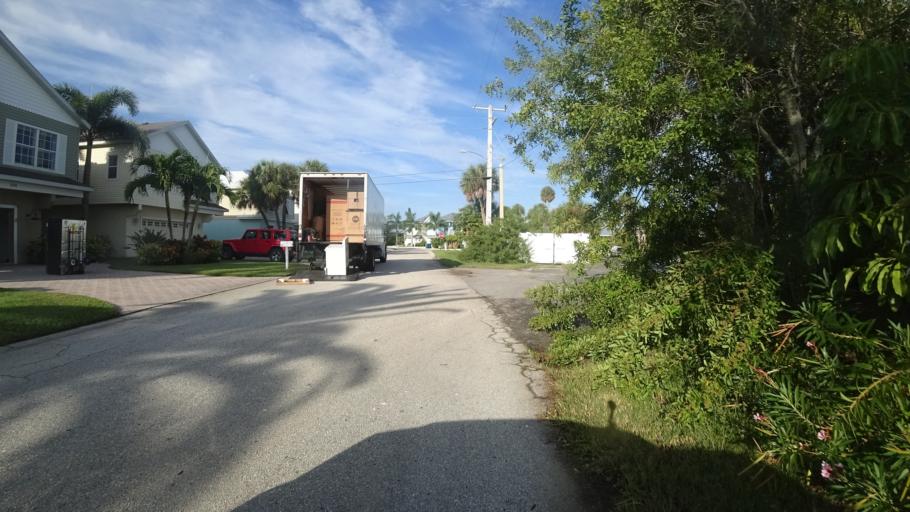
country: US
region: Florida
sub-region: Manatee County
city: Holmes Beach
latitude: 27.5103
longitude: -82.7156
